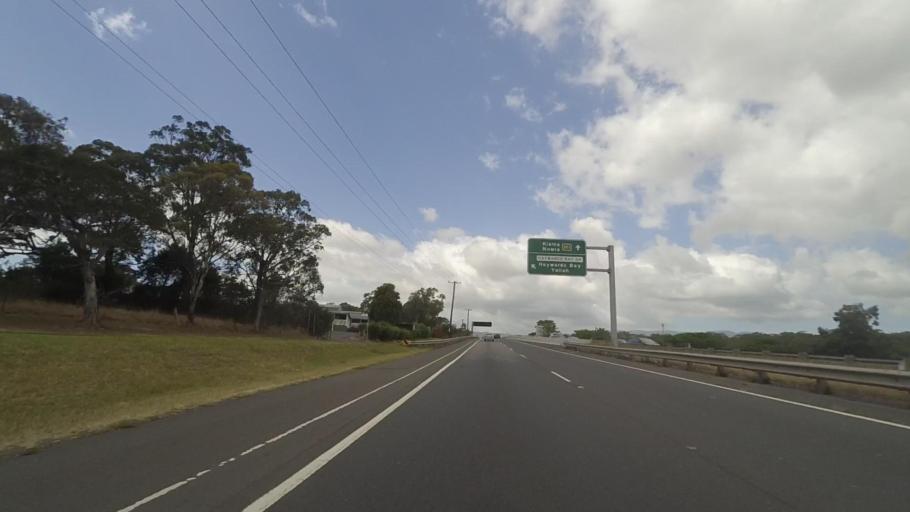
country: AU
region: New South Wales
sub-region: Shellharbour
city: Albion Park Rail
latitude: -34.5348
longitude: 150.7863
